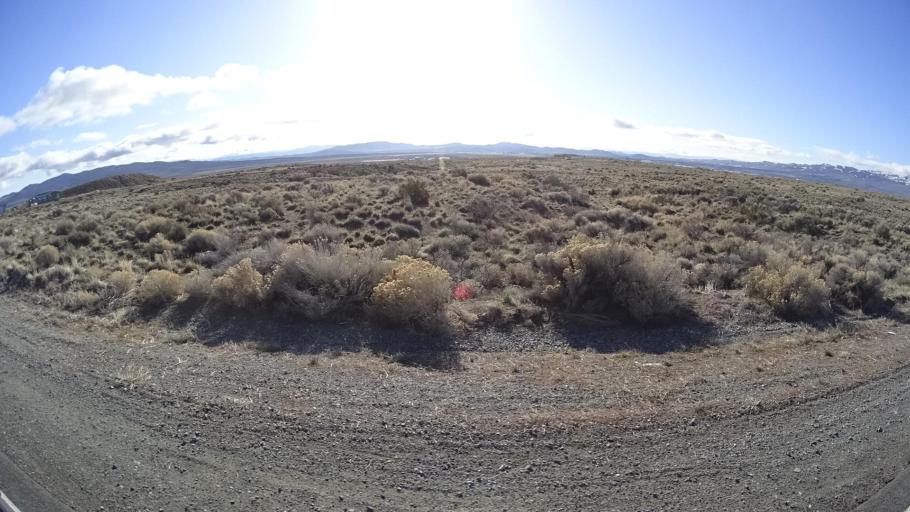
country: US
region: Nevada
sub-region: Washoe County
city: Cold Springs
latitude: 39.6834
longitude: -119.9209
